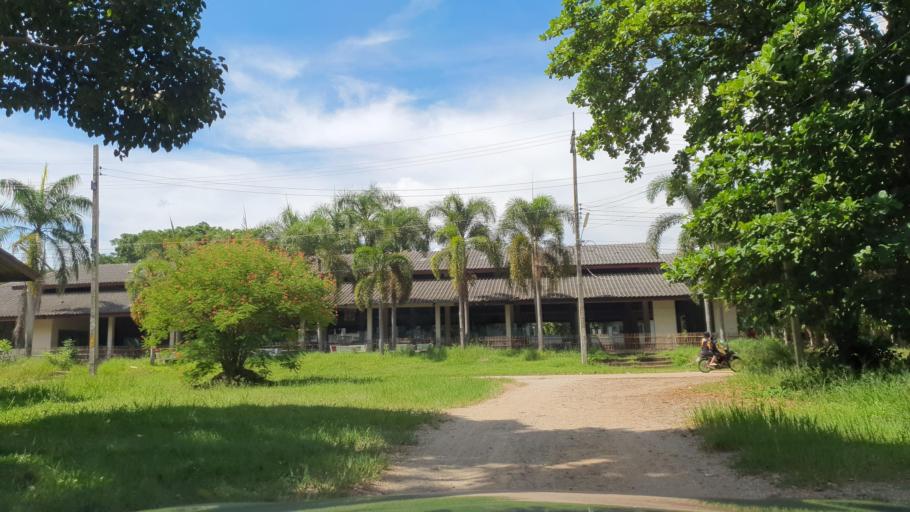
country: TH
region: Chiang Mai
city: San Pa Tong
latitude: 18.5787
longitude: 98.8731
